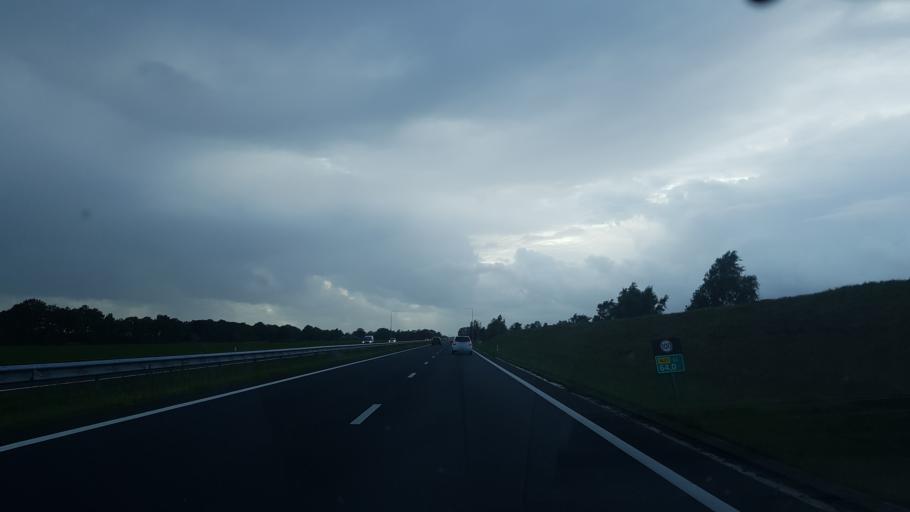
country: NL
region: Friesland
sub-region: Gemeente Smallingerland
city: Oudega
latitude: 53.1478
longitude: 5.9877
